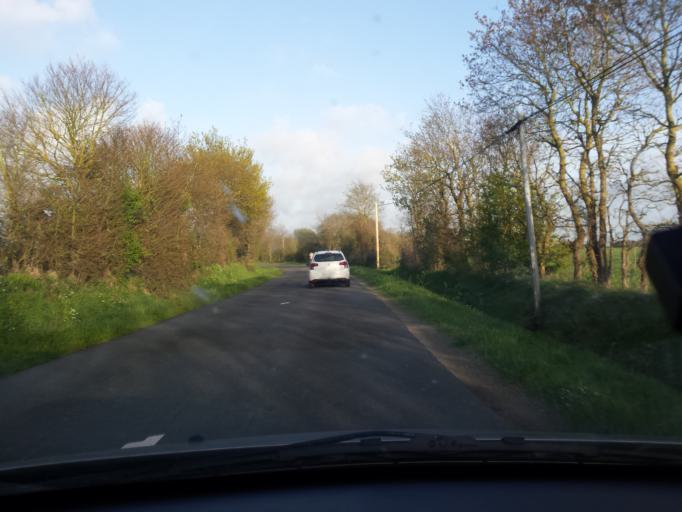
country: FR
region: Pays de la Loire
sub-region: Departement de la Vendee
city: Saint-Mathurin
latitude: 46.5651
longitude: -1.7263
